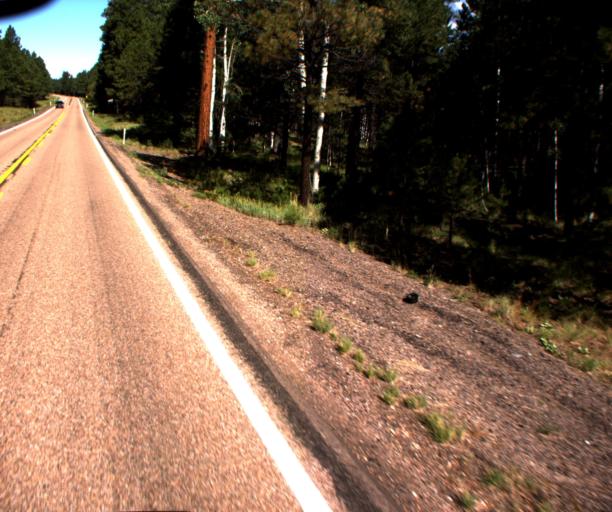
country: US
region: Arizona
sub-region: Navajo County
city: Pinetop-Lakeside
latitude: 34.0388
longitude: -109.6702
